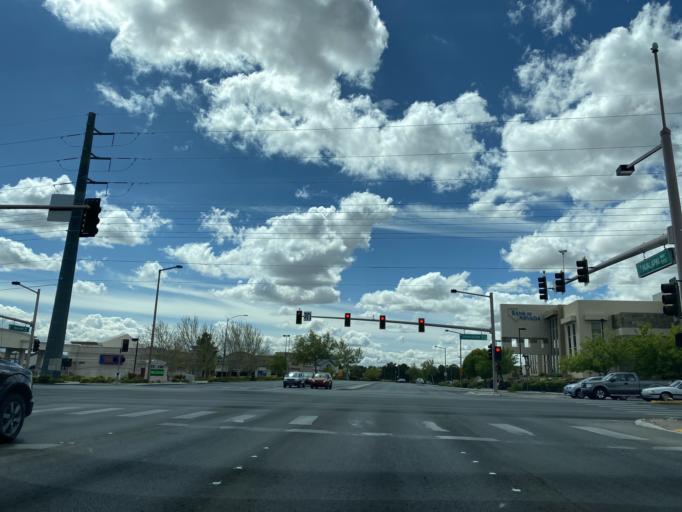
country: US
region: Nevada
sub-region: Clark County
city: Summerlin South
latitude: 36.1593
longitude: -115.3142
